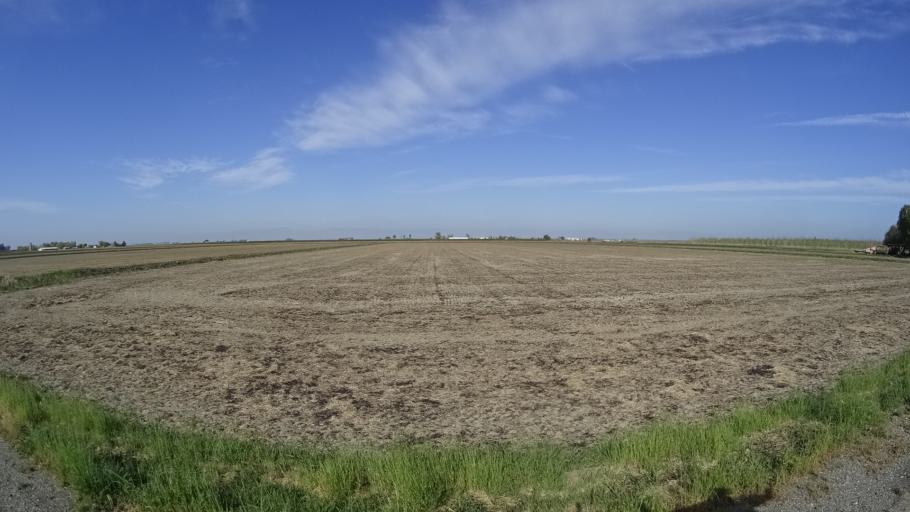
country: US
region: California
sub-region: Glenn County
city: Hamilton City
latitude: 39.6140
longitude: -122.0462
